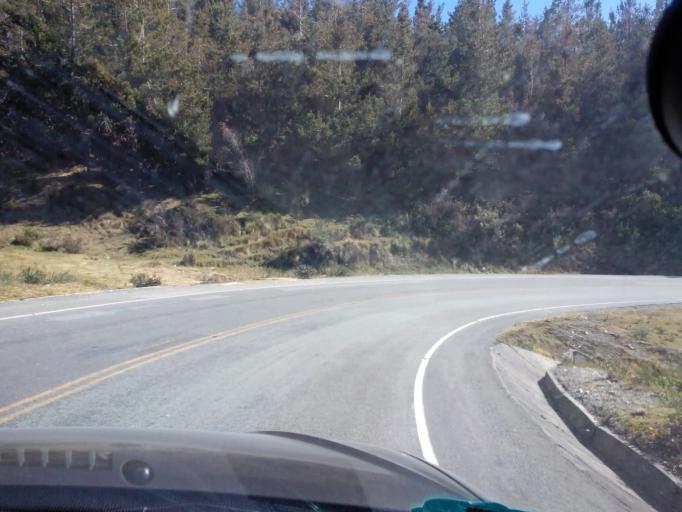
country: PE
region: Apurimac
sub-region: Provincia de Abancay
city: Cachora
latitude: -13.5601
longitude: -72.8206
